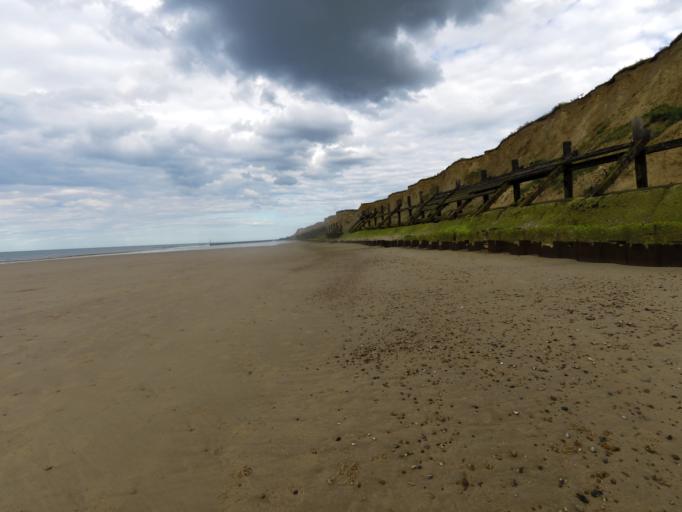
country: GB
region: England
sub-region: Norfolk
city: Sheringham
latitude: 52.9437
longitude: 1.2291
